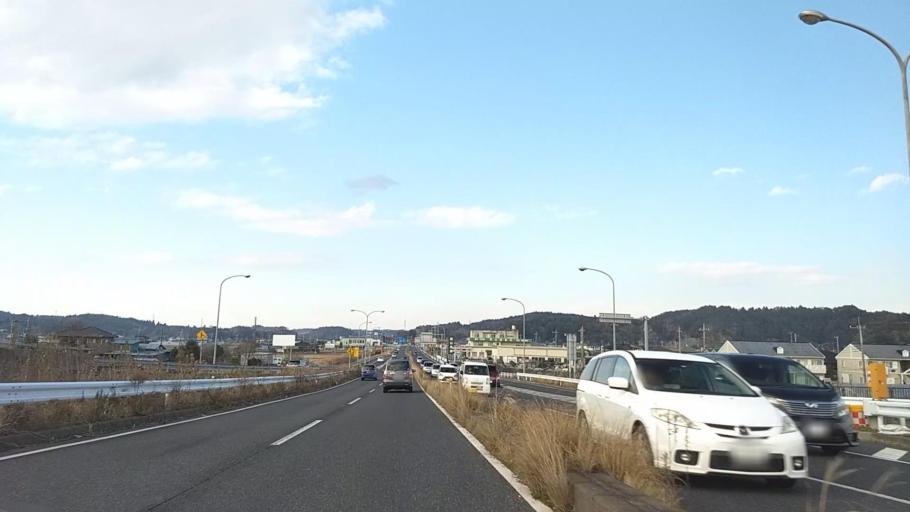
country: JP
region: Chiba
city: Togane
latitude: 35.5523
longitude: 140.3484
